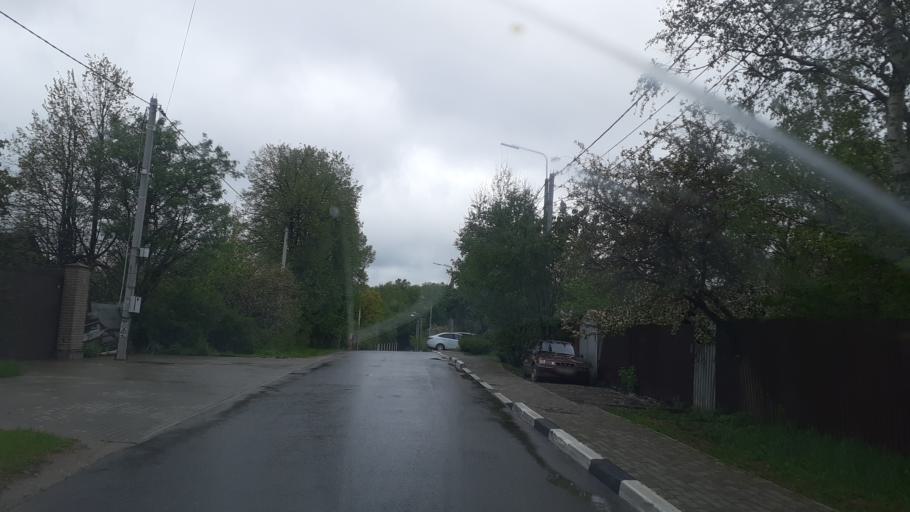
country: RU
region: Moskovskaya
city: Gorki Vtoryye
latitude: 55.7049
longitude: 37.2038
